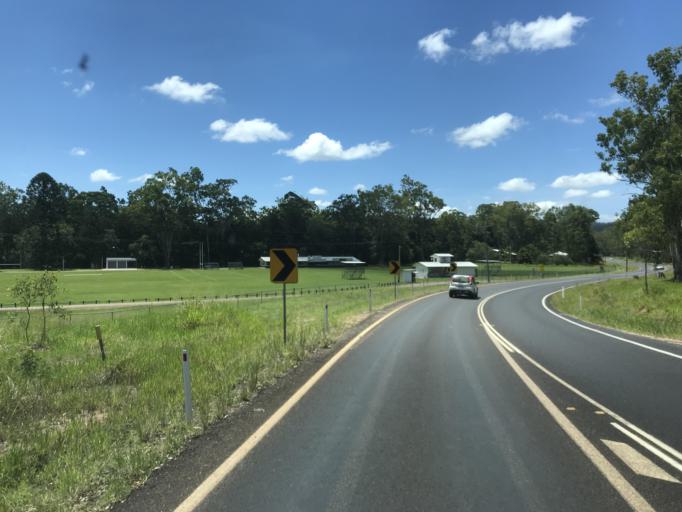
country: AU
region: Queensland
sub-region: Tablelands
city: Atherton
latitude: -17.4111
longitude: 145.3924
